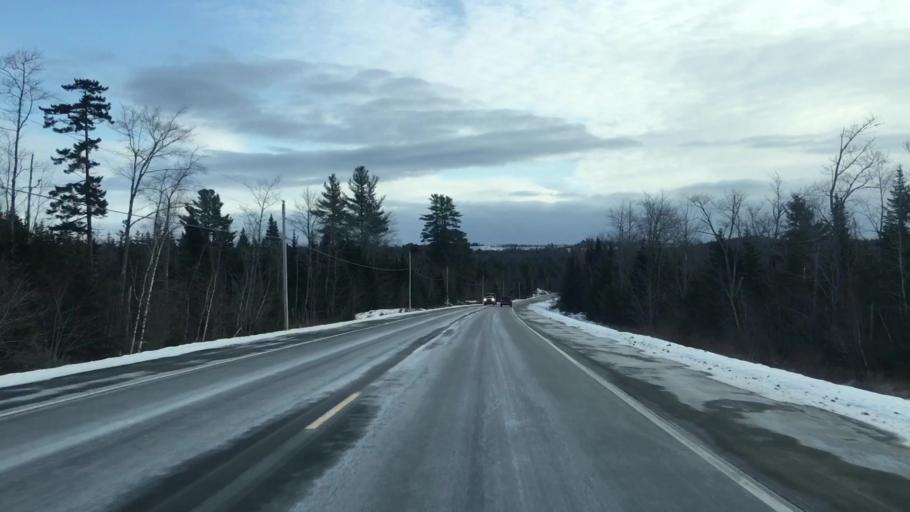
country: US
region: Maine
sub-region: Washington County
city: Machias
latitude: 44.9497
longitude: -67.6885
